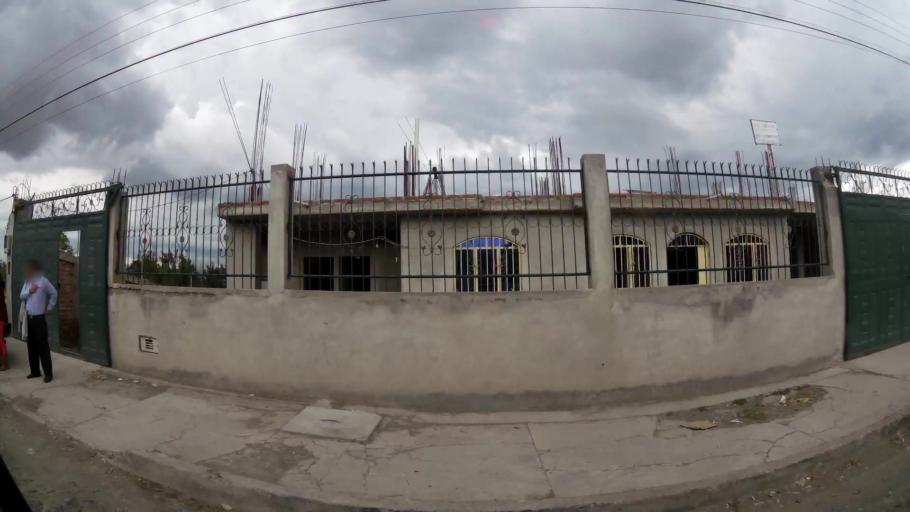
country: EC
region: Tungurahua
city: Ambato
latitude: -1.2682
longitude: -78.6185
